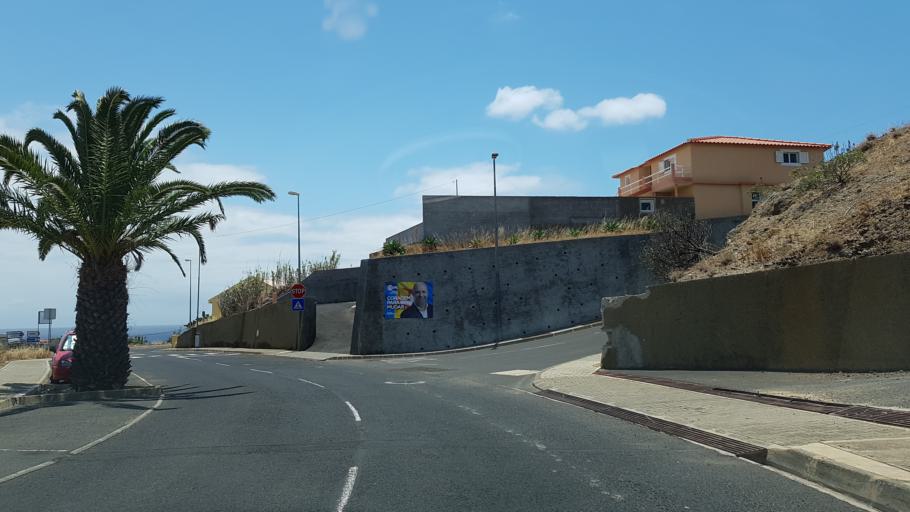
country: PT
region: Madeira
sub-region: Porto Santo
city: Vila de Porto Santo
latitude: 33.0615
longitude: -16.3436
